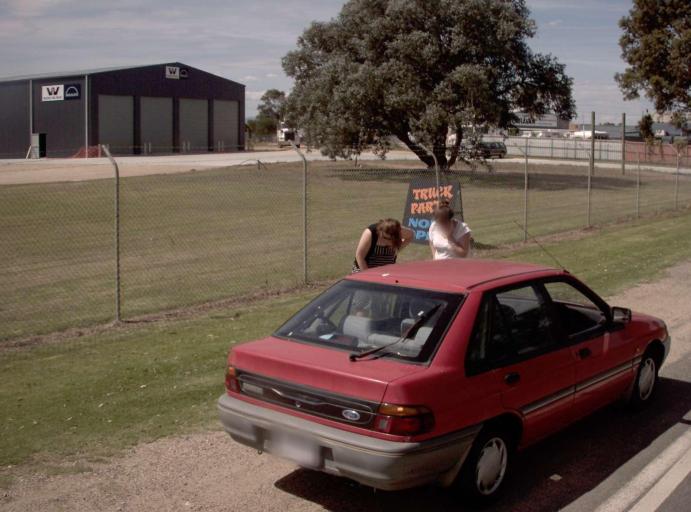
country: AU
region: Victoria
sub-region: East Gippsland
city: Bairnsdale
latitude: -37.8432
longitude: 147.5892
